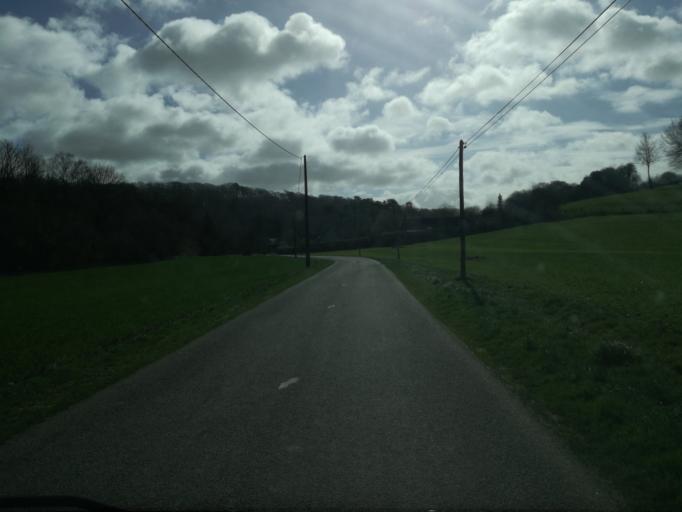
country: FR
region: Haute-Normandie
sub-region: Departement de la Seine-Maritime
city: Yebleron
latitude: 49.6901
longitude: 0.4858
